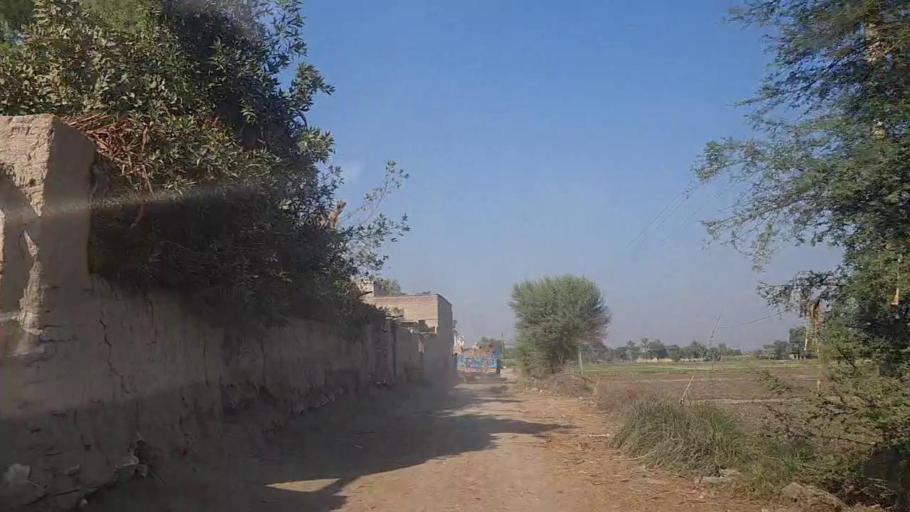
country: PK
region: Sindh
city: Gambat
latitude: 27.3652
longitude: 68.4757
